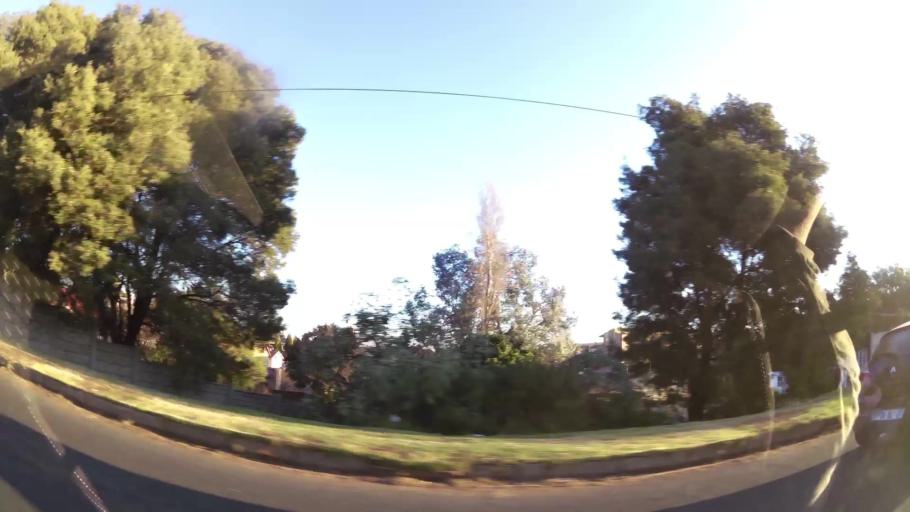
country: ZA
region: Gauteng
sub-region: City of Johannesburg Metropolitan Municipality
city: Roodepoort
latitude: -26.1577
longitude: 27.8869
